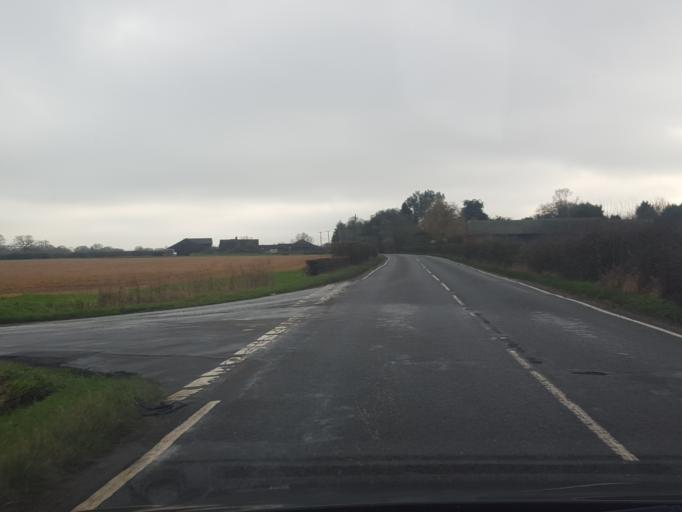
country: GB
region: England
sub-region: Essex
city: West Bergholt
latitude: 51.9317
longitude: 0.8401
